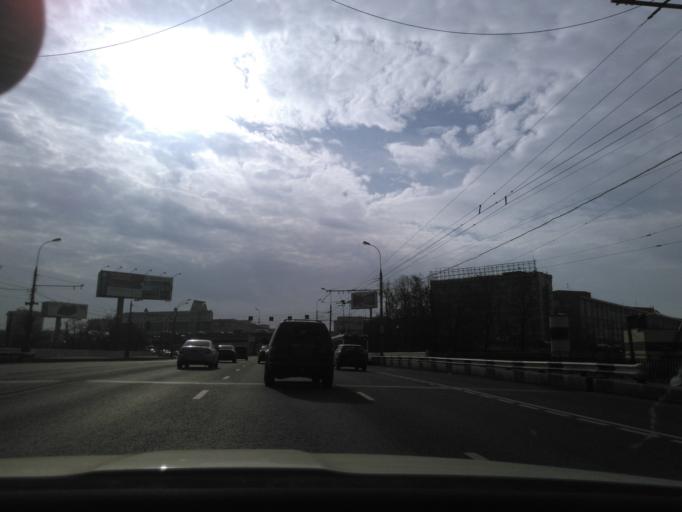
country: RU
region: Moscow
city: Mar'ina Roshcha
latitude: 55.7936
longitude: 37.5860
